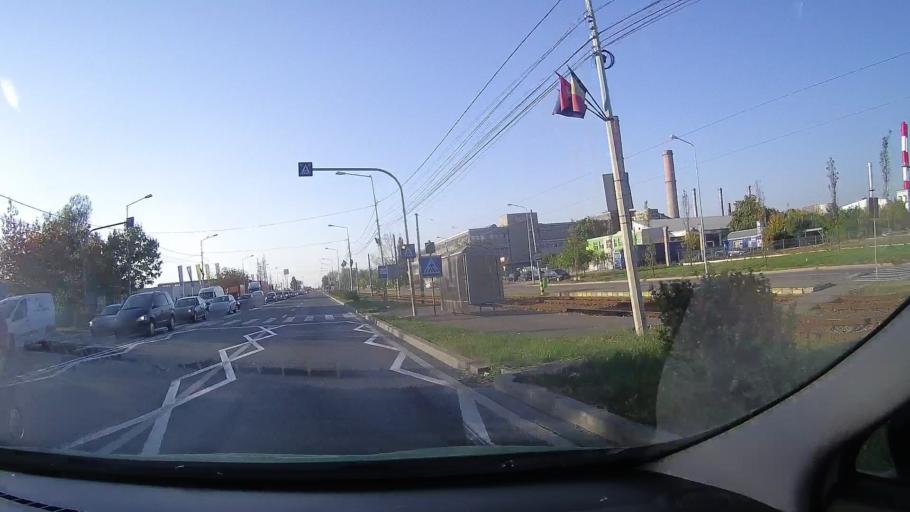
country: RO
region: Bihor
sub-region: Comuna Biharea
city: Oradea
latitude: 47.0795
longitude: 21.8958
